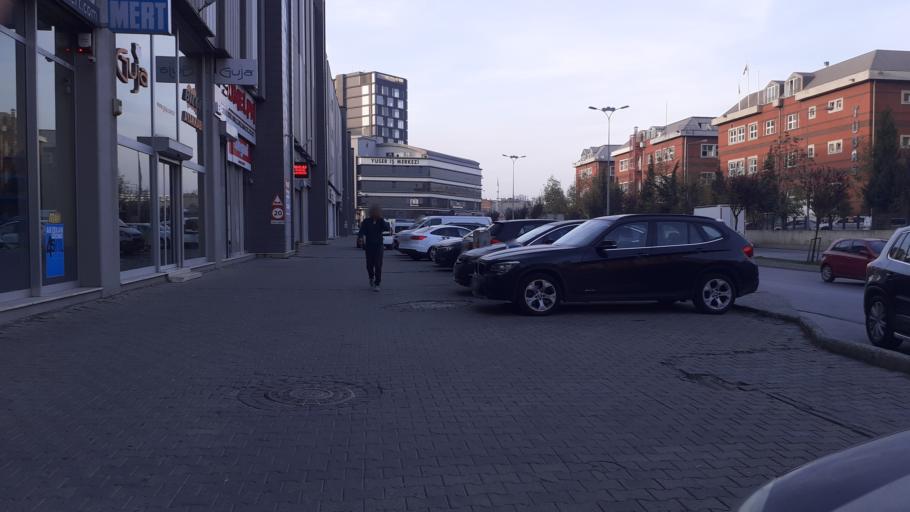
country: TR
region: Istanbul
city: Basaksehir
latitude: 41.0715
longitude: 28.7945
